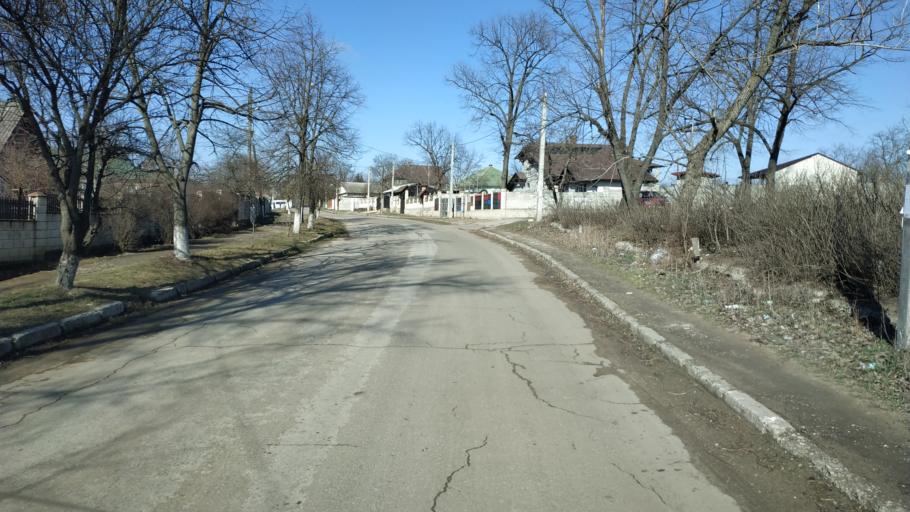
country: MD
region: Hincesti
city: Hincesti
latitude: 46.9733
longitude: 28.5783
